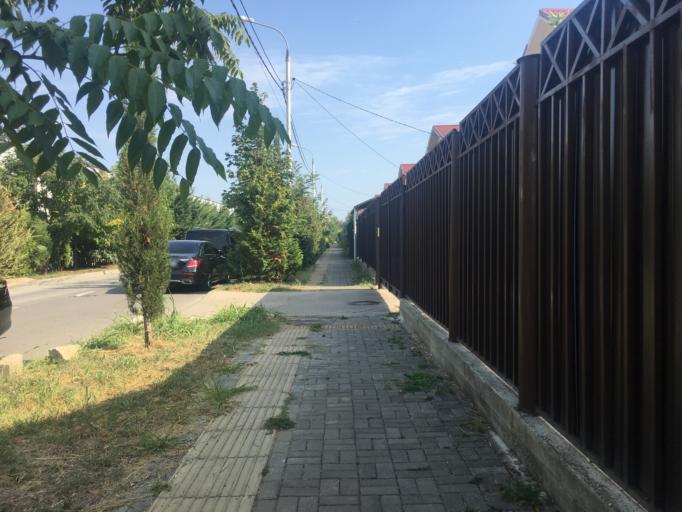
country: RU
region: Krasnodarskiy
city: Vysokoye
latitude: 43.3957
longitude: 40.0002
